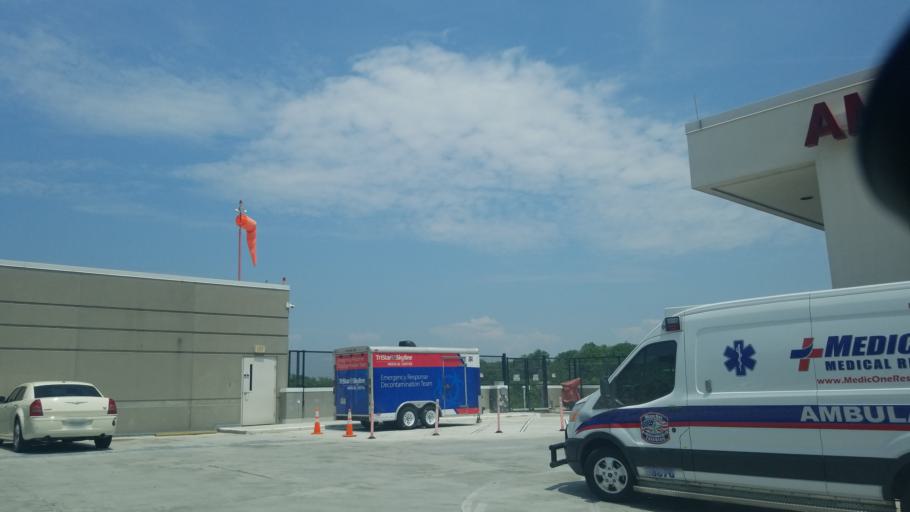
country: US
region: Tennessee
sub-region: Davidson County
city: Goodlettsville
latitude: 36.2458
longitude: -86.7499
